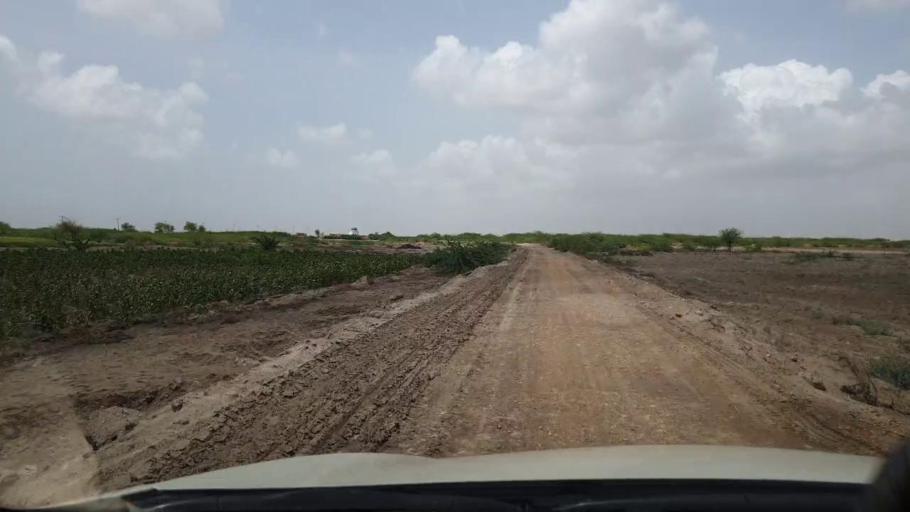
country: PK
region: Sindh
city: Kadhan
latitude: 24.3669
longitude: 68.8501
